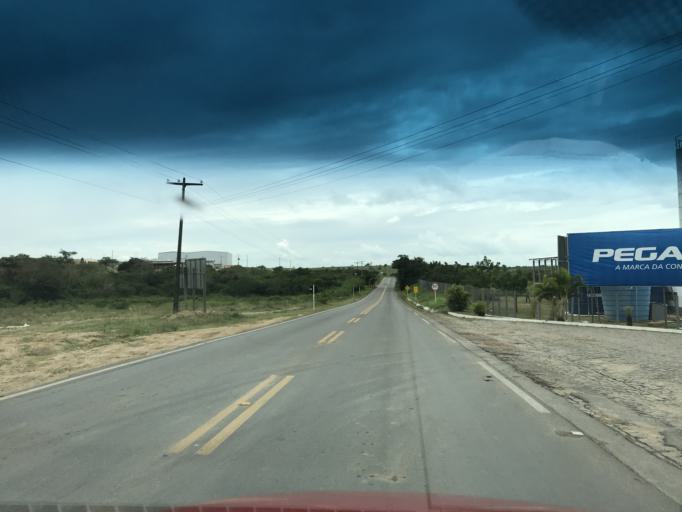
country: BR
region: Bahia
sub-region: Castro Alves
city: Castro Alves
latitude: -12.7600
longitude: -39.4188
